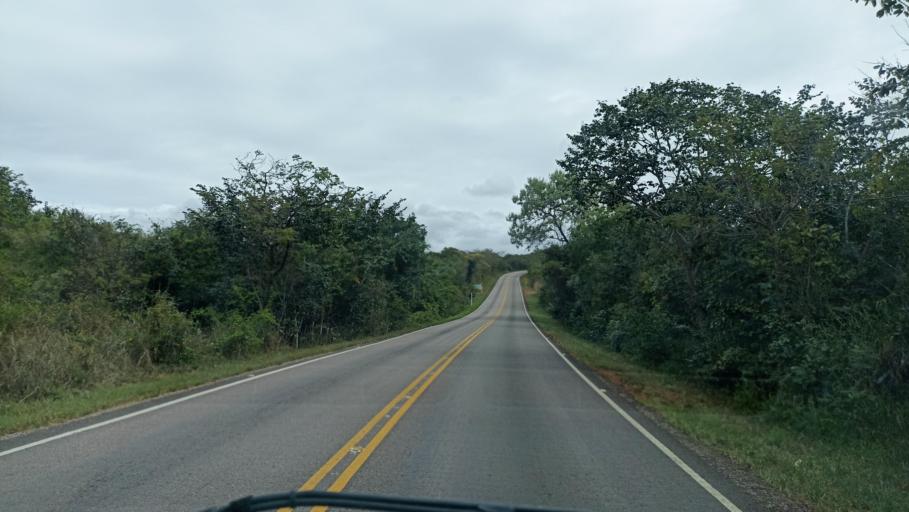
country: BR
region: Bahia
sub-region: Andarai
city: Vera Cruz
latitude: -12.9265
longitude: -41.2335
